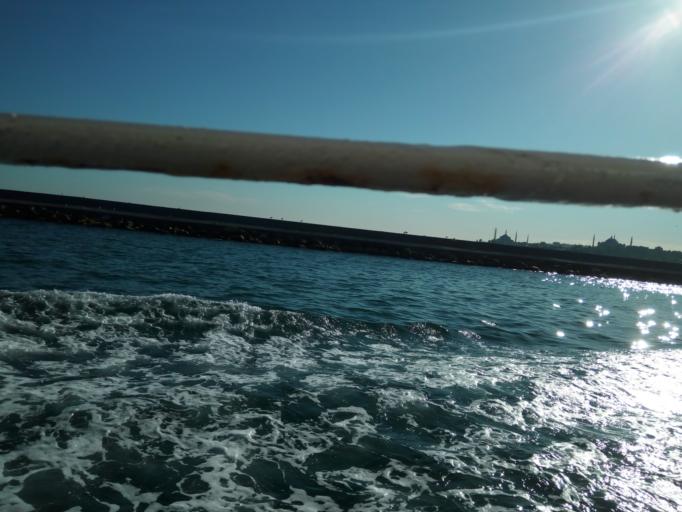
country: TR
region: Istanbul
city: UEskuedar
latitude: 41.0074
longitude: 29.0038
